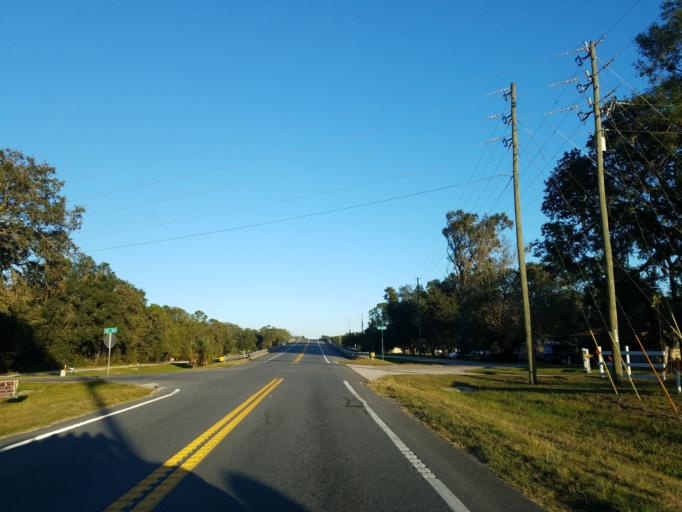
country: US
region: Florida
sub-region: Sumter County
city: Bushnell
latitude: 28.6578
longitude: -82.1539
